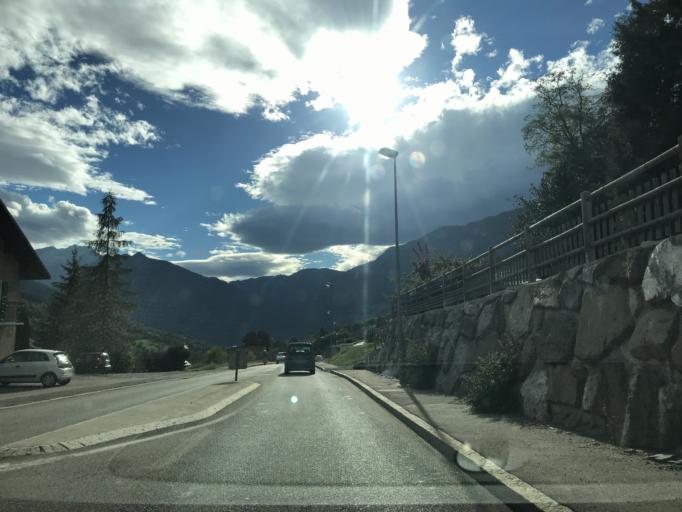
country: FR
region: Rhone-Alpes
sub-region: Departement de la Haute-Savoie
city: Saint-Jean-de-Sixt
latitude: 45.9096
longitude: 6.3681
